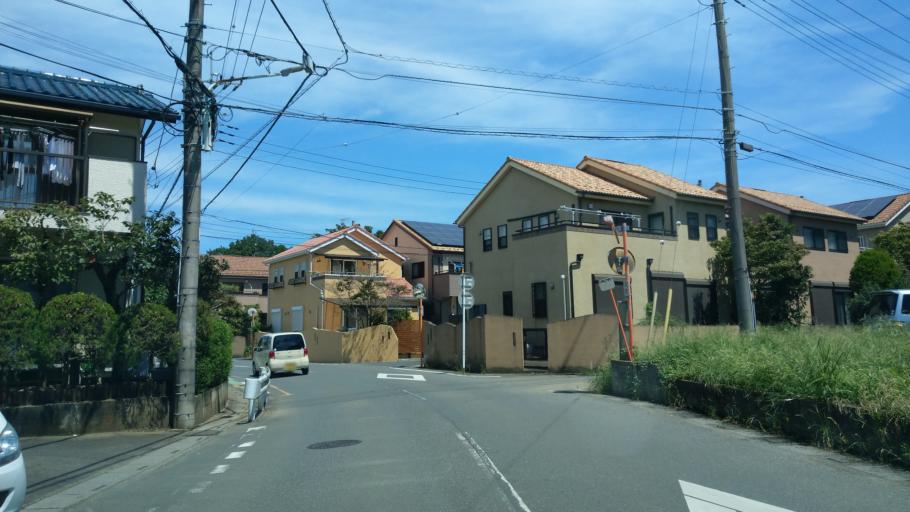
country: JP
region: Saitama
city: Ageoshimo
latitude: 35.9287
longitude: 139.5648
